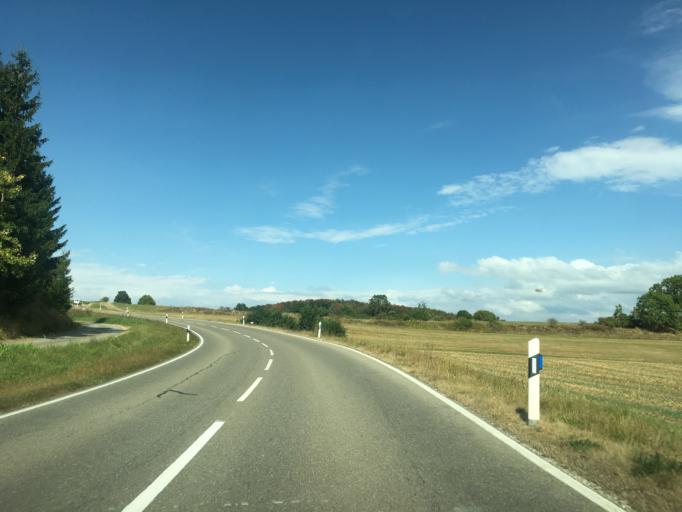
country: DE
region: Baden-Wuerttemberg
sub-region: Tuebingen Region
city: Trochtelfingen
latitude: 48.3614
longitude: 9.1993
